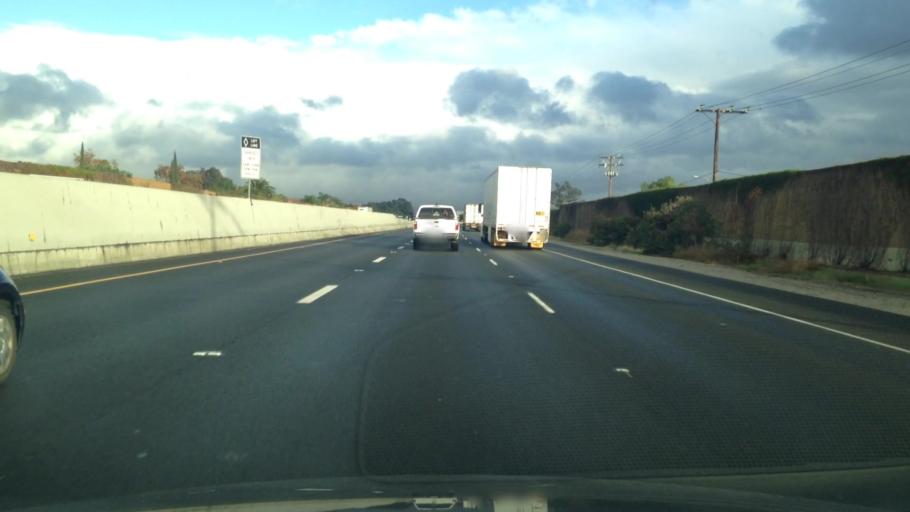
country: US
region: California
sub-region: Riverside County
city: Moreno Valley
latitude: 33.9391
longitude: -117.2174
